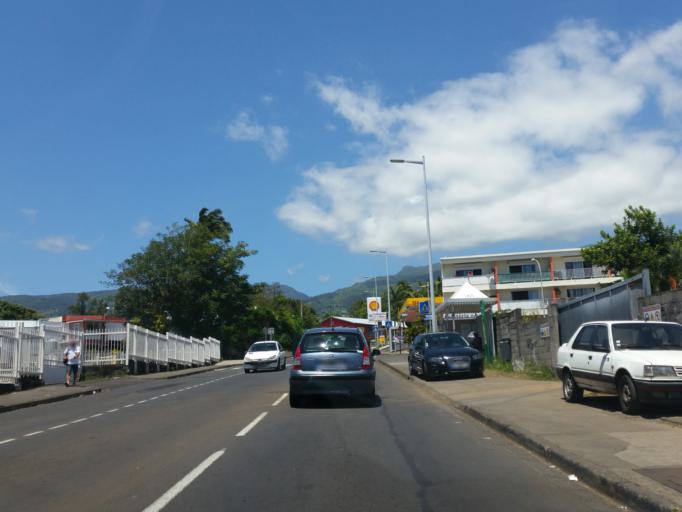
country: RE
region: Reunion
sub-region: Reunion
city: Saint-Denis
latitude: -20.9026
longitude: 55.4921
